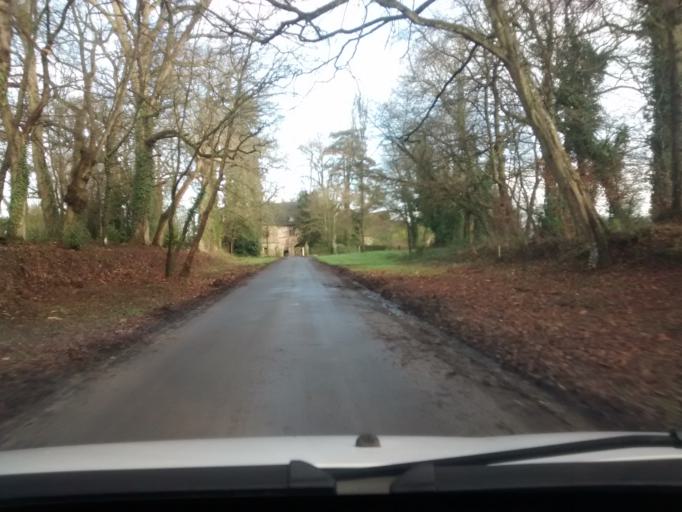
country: FR
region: Brittany
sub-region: Departement d'Ille-et-Vilaine
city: Vezin-le-Coquet
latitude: 48.1300
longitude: -1.7350
